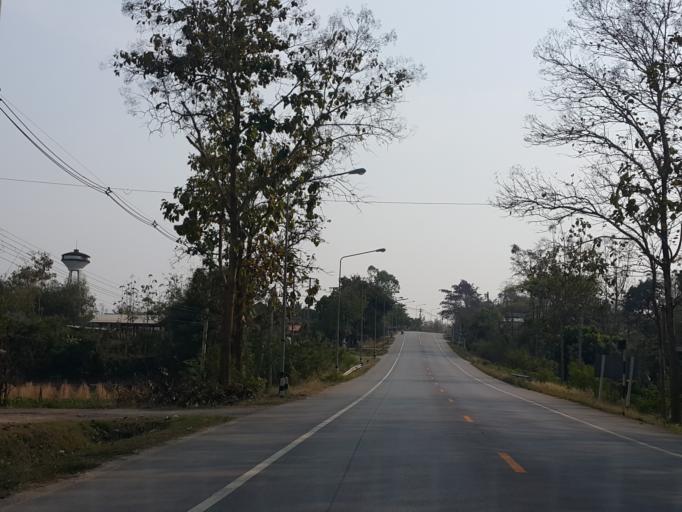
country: TH
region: Lampang
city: Chae Hom
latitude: 18.7177
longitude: 99.5611
